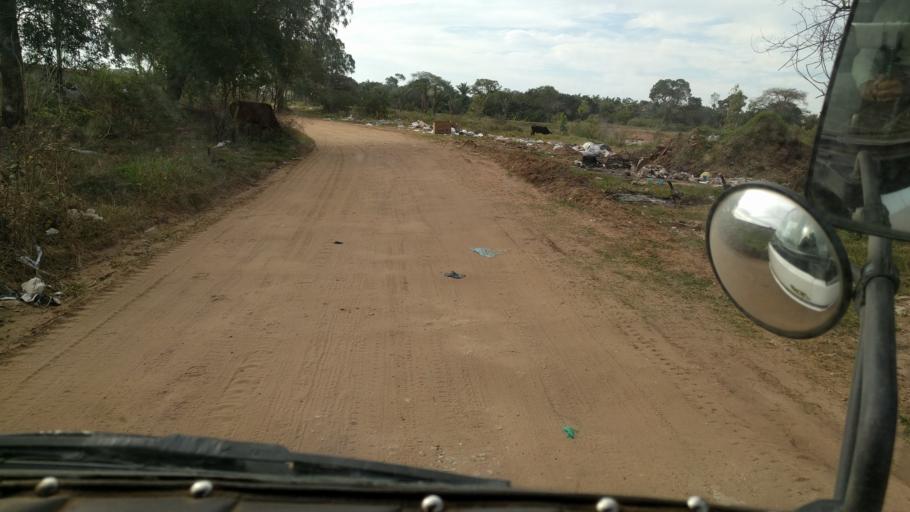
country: BO
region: Santa Cruz
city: Santa Cruz de la Sierra
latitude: -17.6816
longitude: -63.1426
